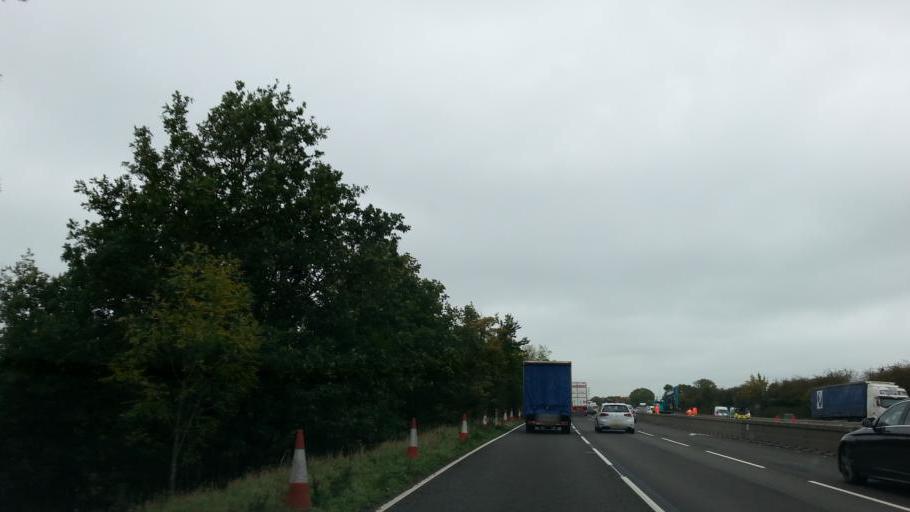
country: GB
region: England
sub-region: Staffordshire
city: Stone
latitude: 52.9064
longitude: -2.1919
